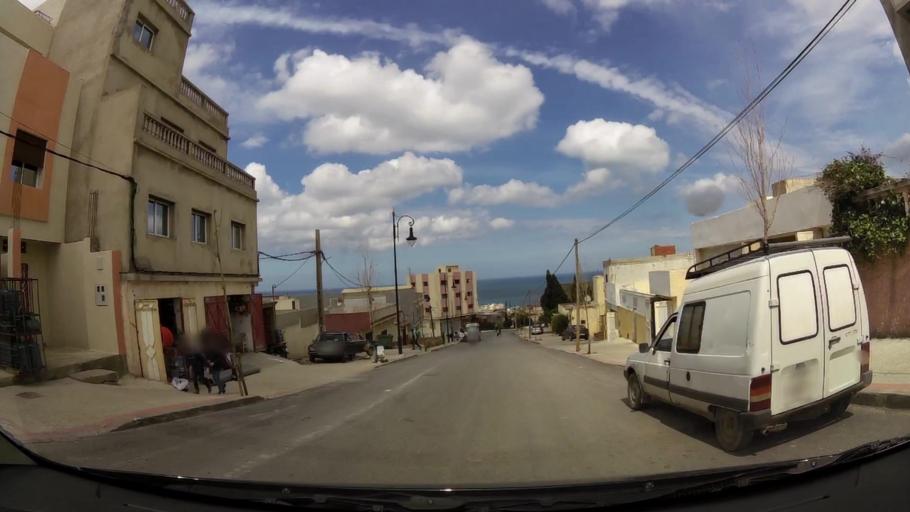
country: MA
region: Tanger-Tetouan
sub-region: Tanger-Assilah
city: Tangier
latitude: 35.7775
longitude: -5.7537
